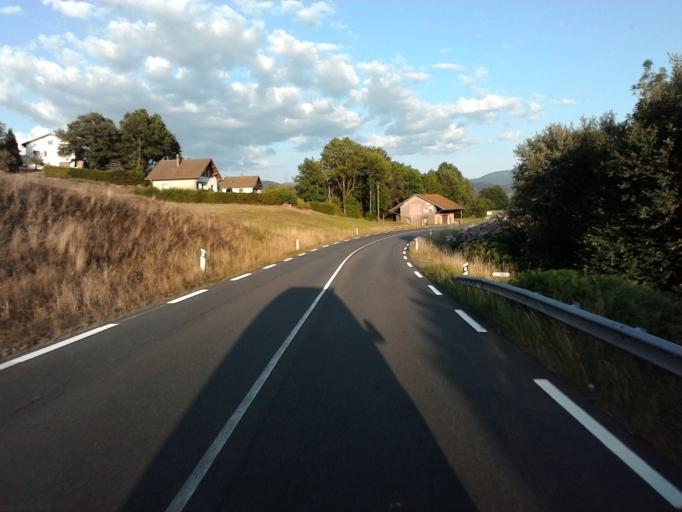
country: FR
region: Lorraine
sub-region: Departement des Vosges
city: Ramonchamp
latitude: 47.9014
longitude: 6.7192
